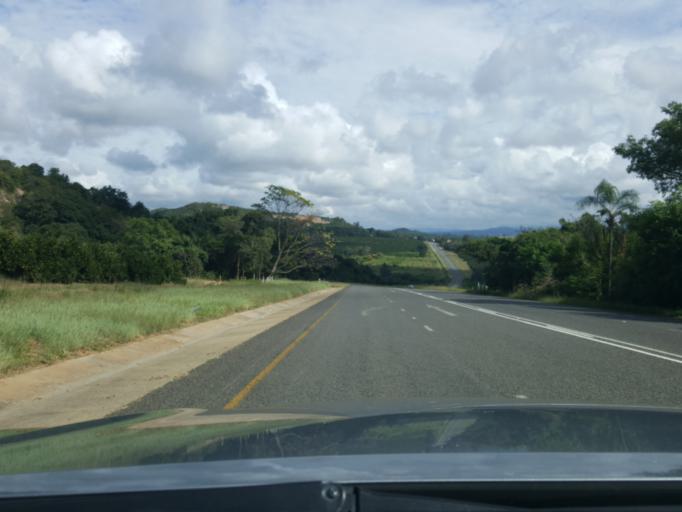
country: ZA
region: Mpumalanga
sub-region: Ehlanzeni District
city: Nelspruit
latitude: -25.4727
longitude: 31.0627
